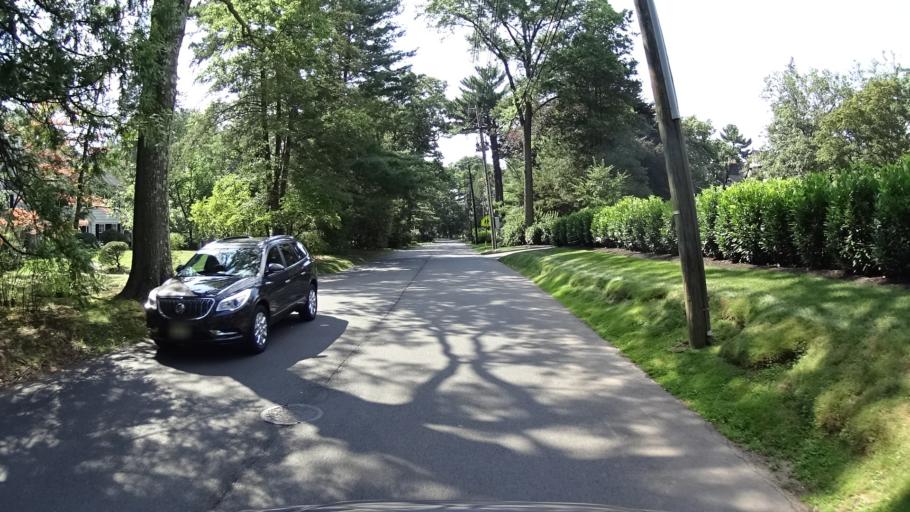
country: US
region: New Jersey
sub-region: Union County
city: Westfield
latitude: 40.6670
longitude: -74.3378
